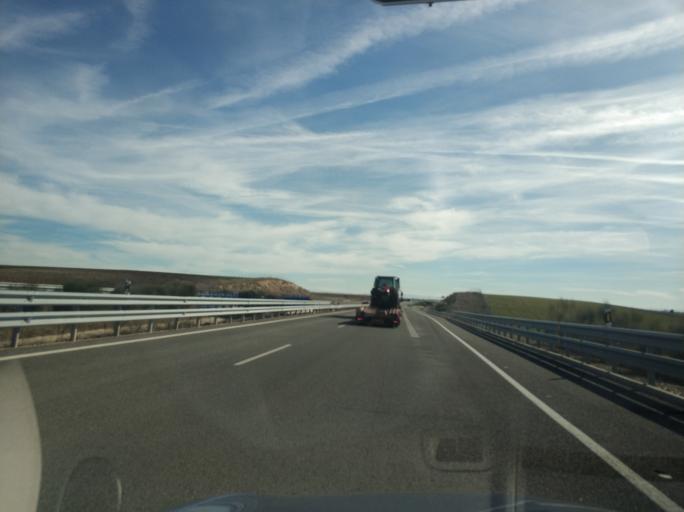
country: ES
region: Castille and Leon
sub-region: Provincia de Salamanca
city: Calzada de Valdunciel
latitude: 41.0914
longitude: -5.6931
